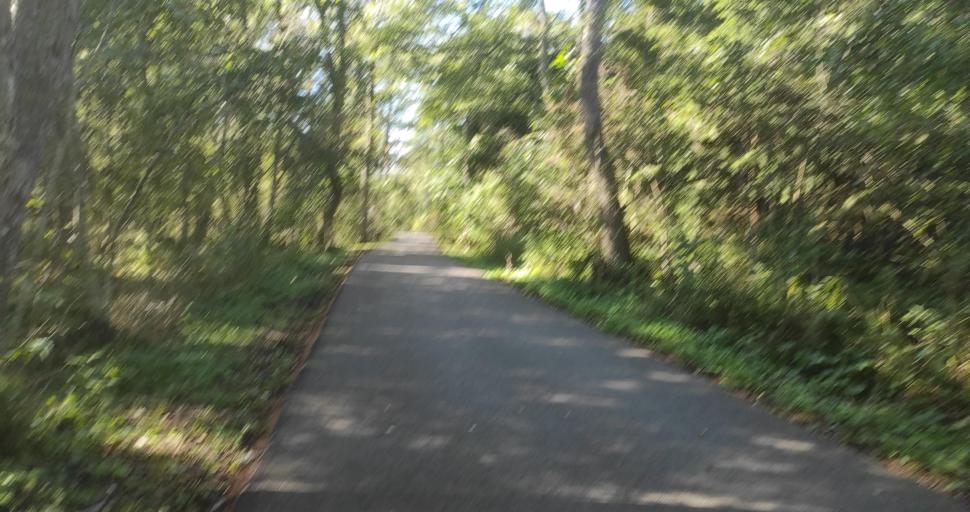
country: LT
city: Nida
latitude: 55.3065
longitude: 20.9824
